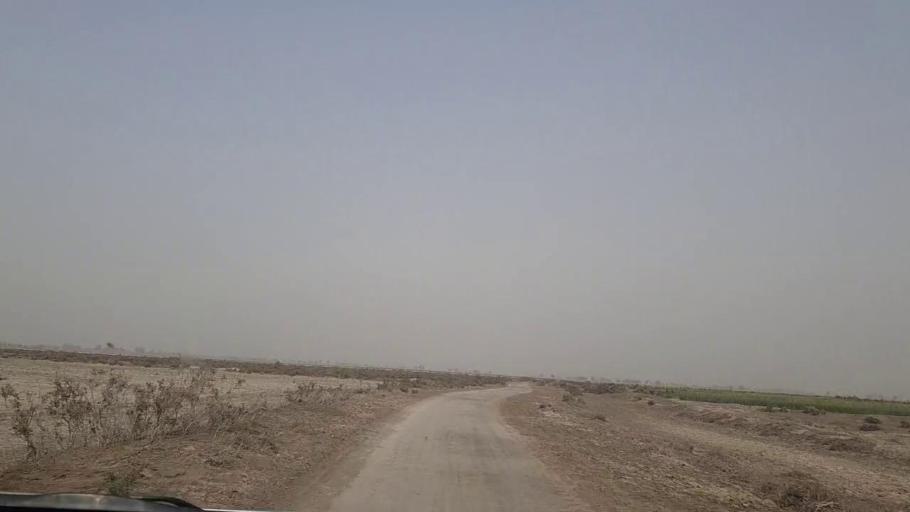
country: PK
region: Sindh
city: Pithoro
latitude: 25.4643
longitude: 69.2611
